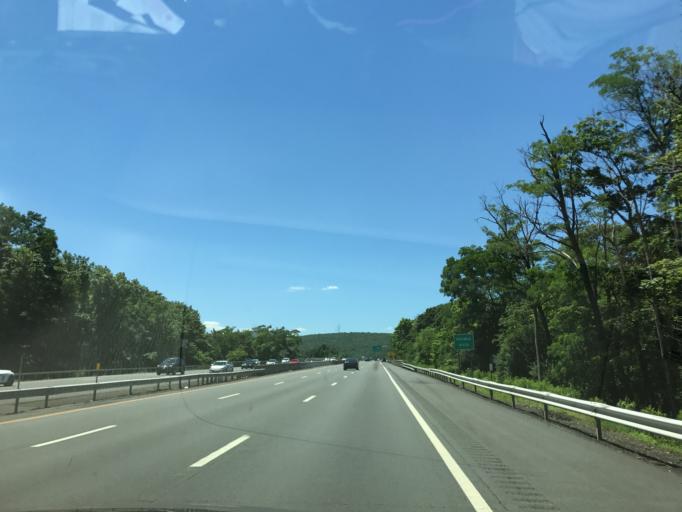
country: US
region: New York
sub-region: Rockland County
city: Suffern
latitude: 41.1208
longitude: -74.1442
